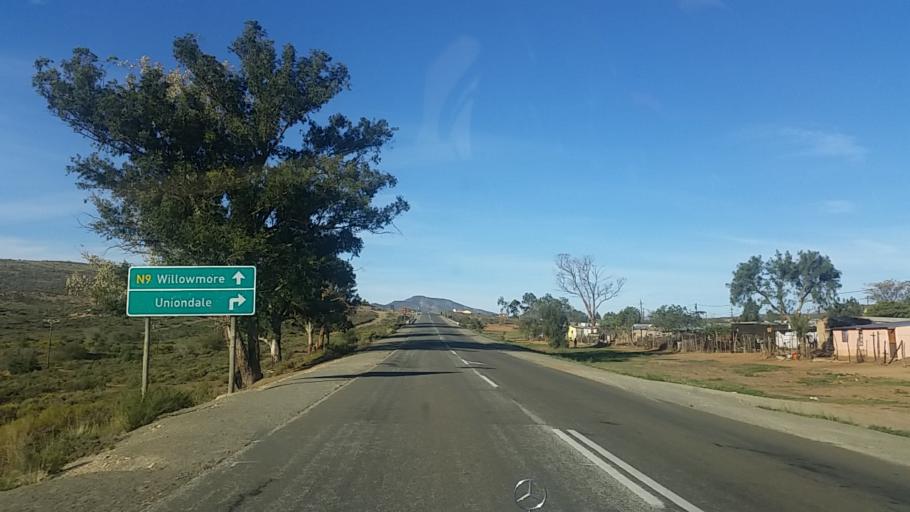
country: ZA
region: Western Cape
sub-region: Eden District Municipality
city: Knysna
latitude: -33.6629
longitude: 23.1082
